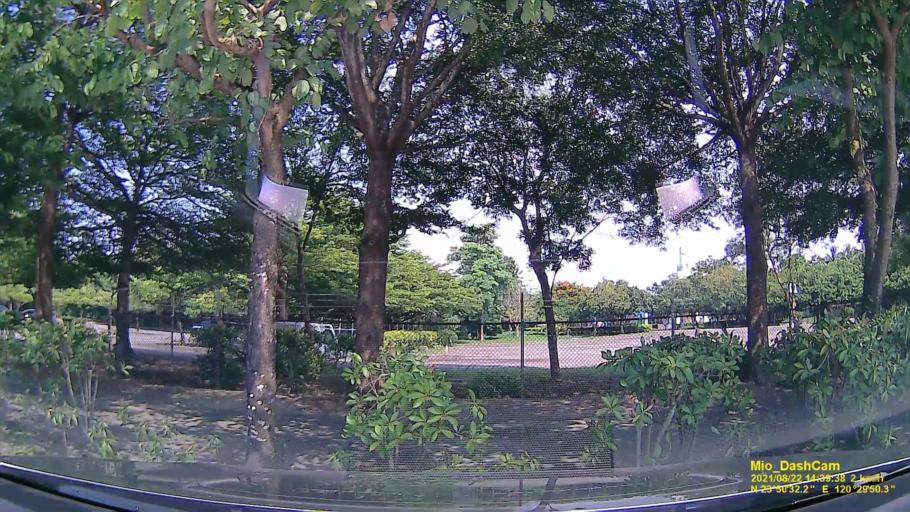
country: TW
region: Taiwan
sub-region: Yunlin
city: Douliu
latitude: 23.8423
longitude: 120.4973
